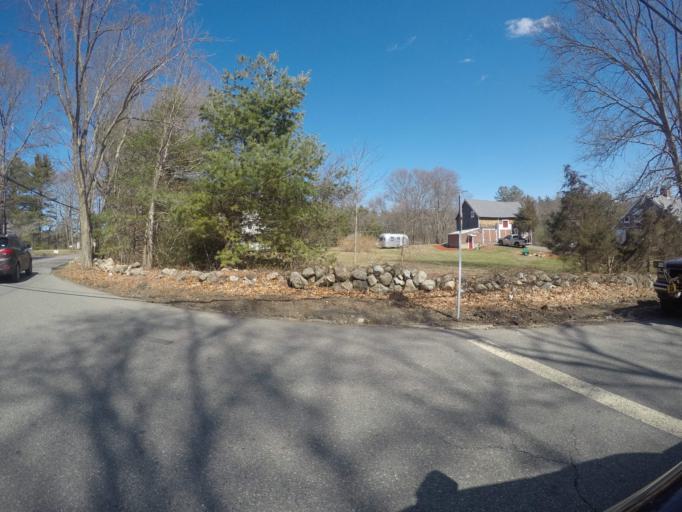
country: US
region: Massachusetts
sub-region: Bristol County
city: Easton
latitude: 42.0123
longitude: -71.0983
